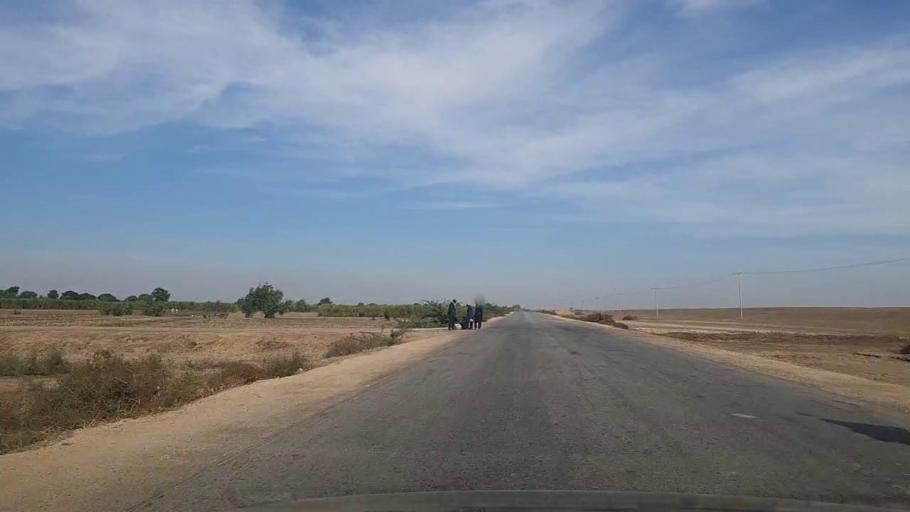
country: PK
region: Sindh
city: Daro Mehar
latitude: 24.9420
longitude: 68.1097
